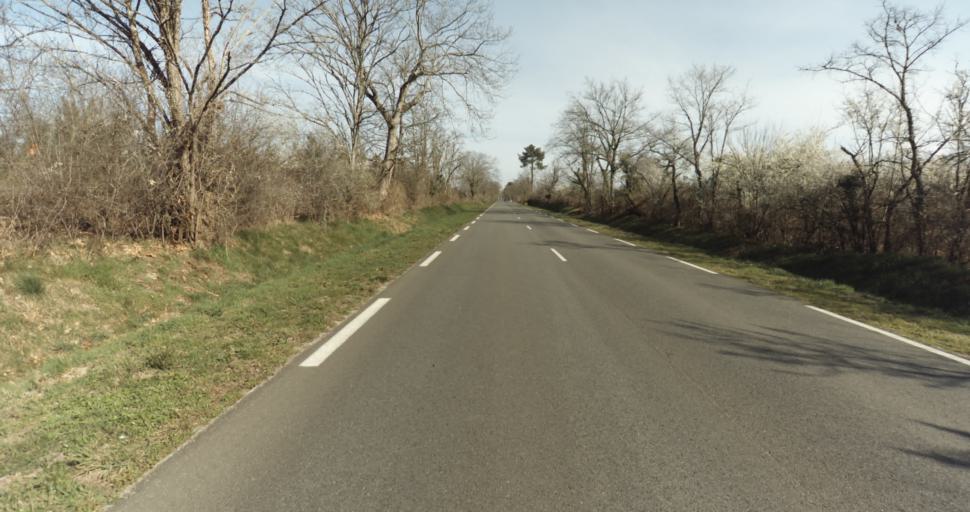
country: FR
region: Aquitaine
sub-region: Departement des Landes
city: Roquefort
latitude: 44.0703
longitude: -0.3148
